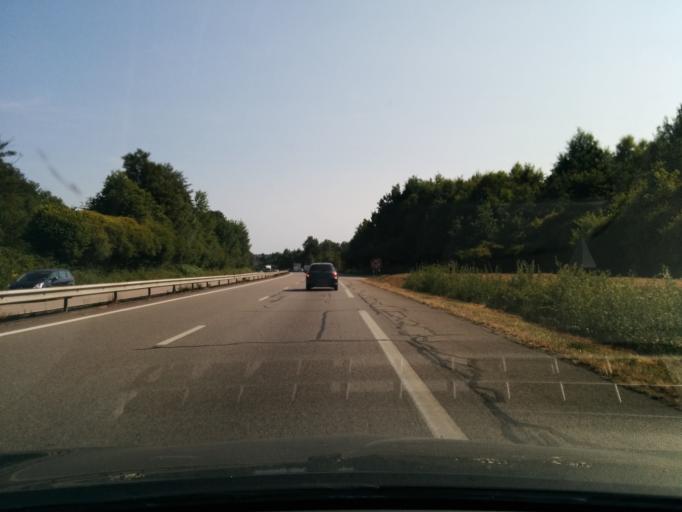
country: FR
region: Limousin
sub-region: Departement de la Haute-Vienne
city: Rilhac-Rancon
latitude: 45.9117
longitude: 1.2925
